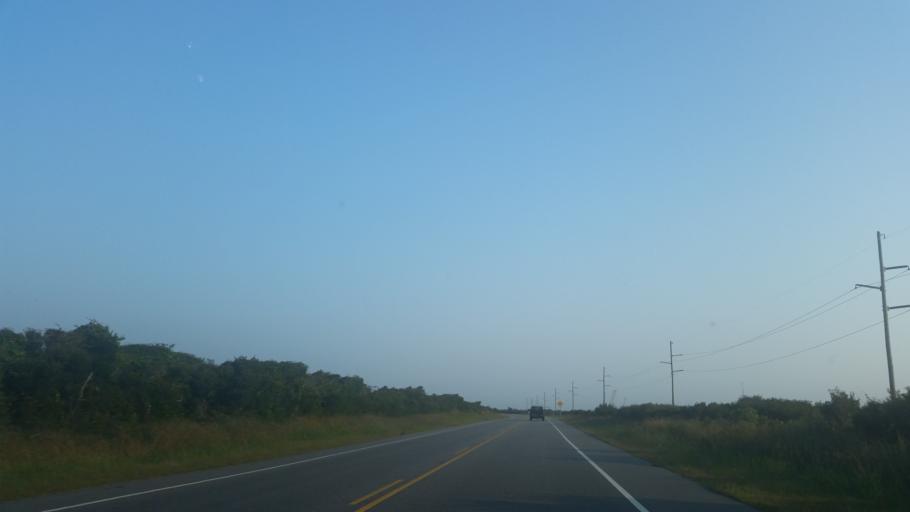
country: US
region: North Carolina
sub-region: Dare County
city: Wanchese
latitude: 35.8118
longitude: -75.5509
